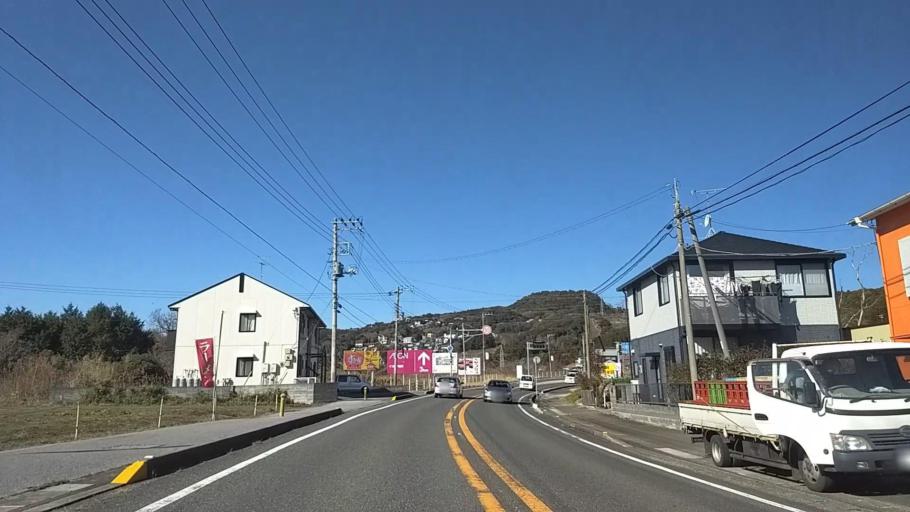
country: JP
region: Chiba
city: Kawaguchi
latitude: 35.0879
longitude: 140.0911
